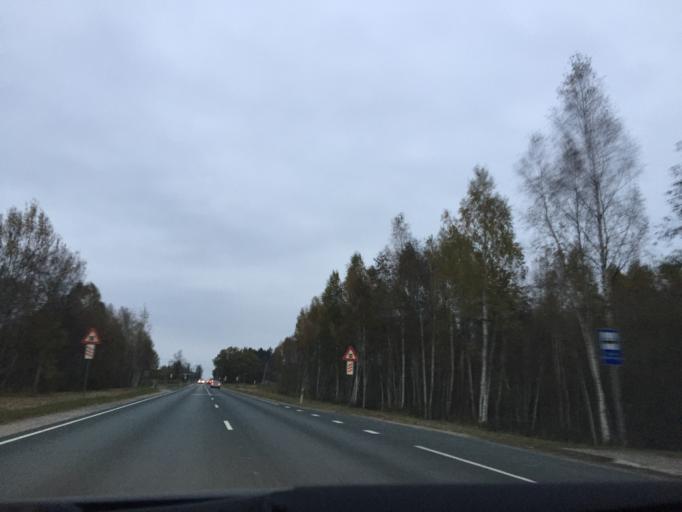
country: LV
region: Ozolnieku
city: Ozolnieki
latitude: 56.7230
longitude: 23.8477
